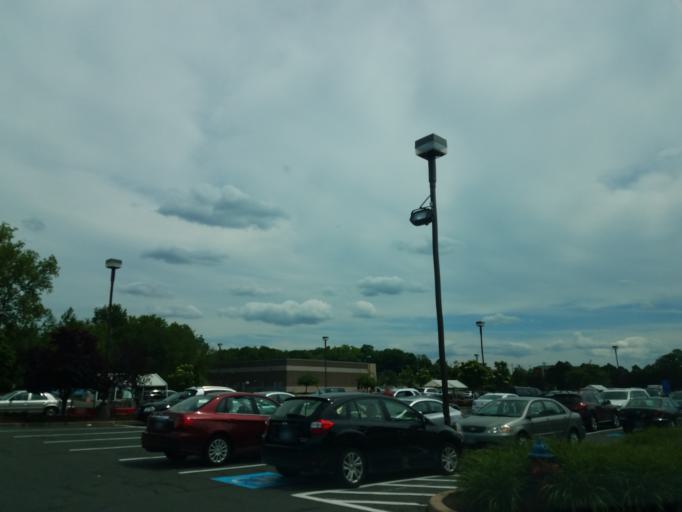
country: US
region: Connecticut
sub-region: Hartford County
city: Newington
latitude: 41.6693
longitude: -72.7206
